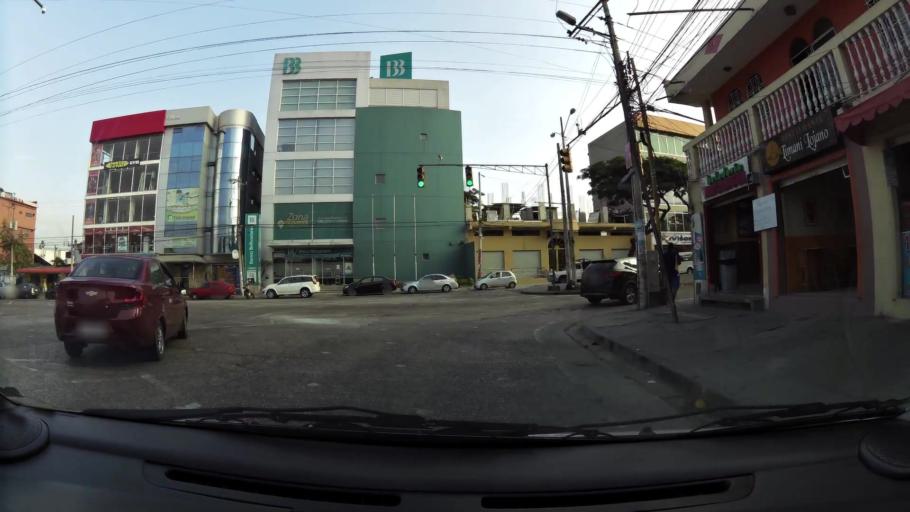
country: EC
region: Guayas
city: Eloy Alfaro
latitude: -2.1332
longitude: -79.9040
